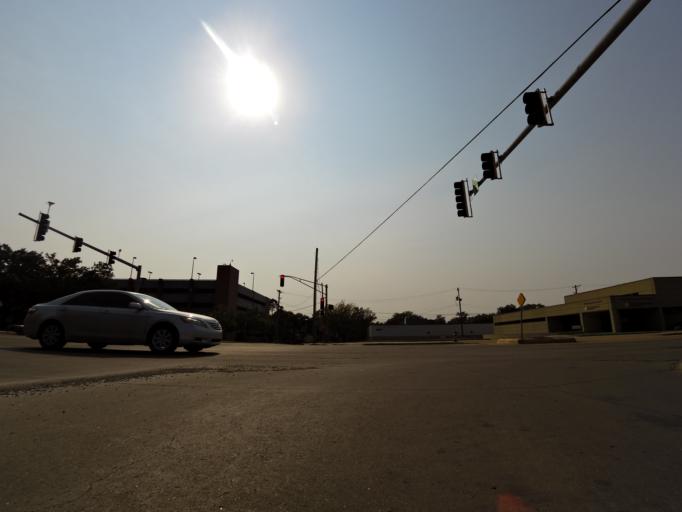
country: US
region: Kansas
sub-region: Sedgwick County
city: Wichita
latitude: 37.6974
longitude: -97.2988
